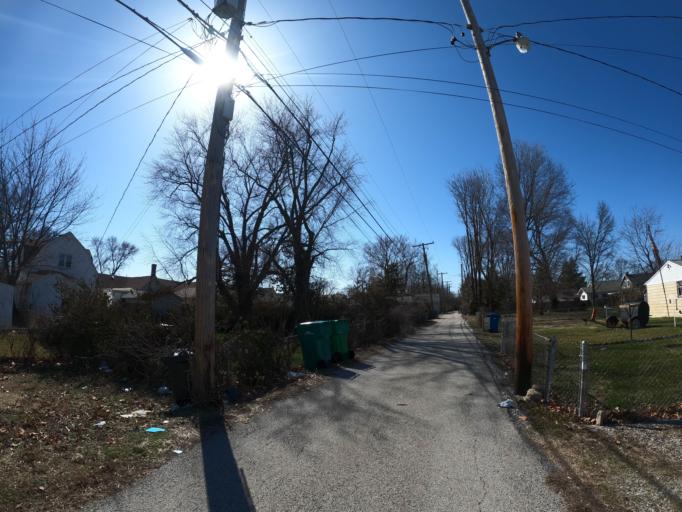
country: US
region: Illinois
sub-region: Sangamon County
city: Springfield
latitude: 39.8070
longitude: -89.6600
